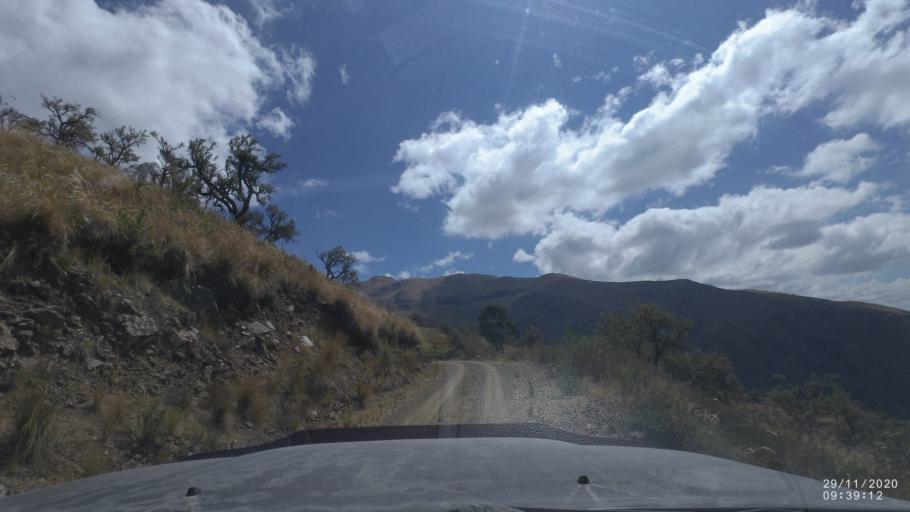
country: BO
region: Cochabamba
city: Cochabamba
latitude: -17.3054
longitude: -66.1841
